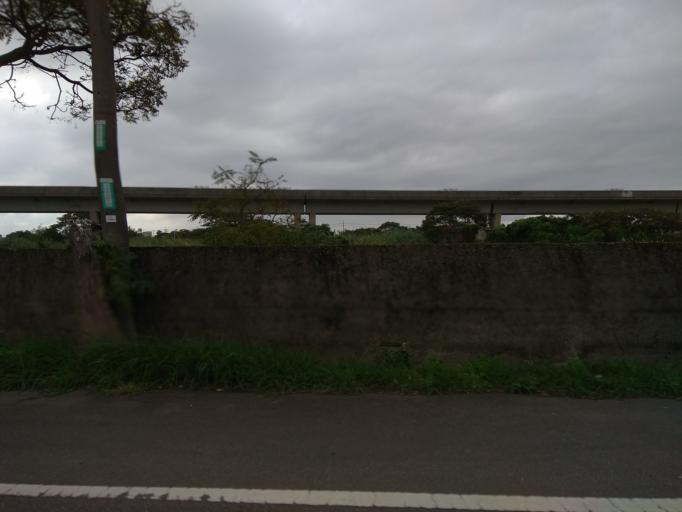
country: TW
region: Taiwan
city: Taoyuan City
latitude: 25.0487
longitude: 121.2141
